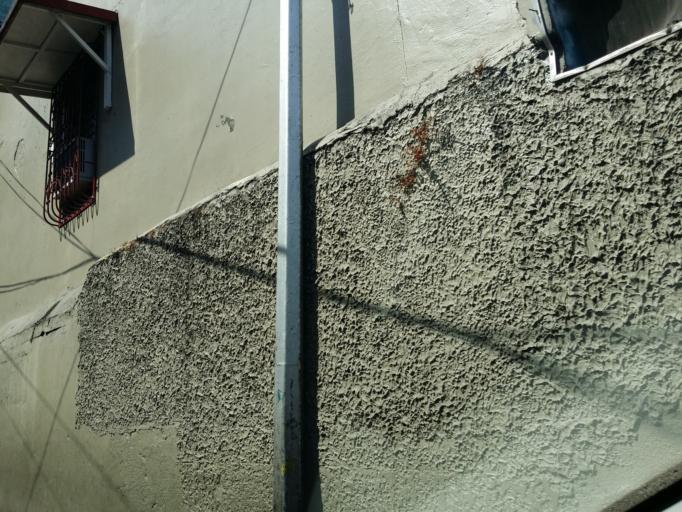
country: PH
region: Metro Manila
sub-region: San Juan
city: San Juan
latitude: 14.5862
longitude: 121.0228
